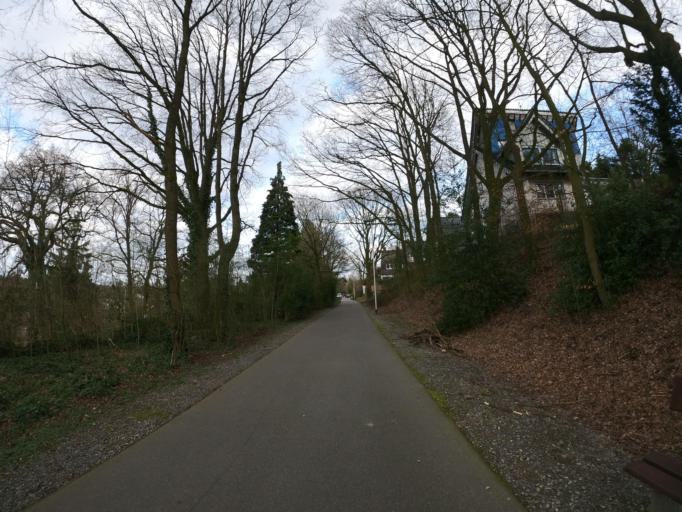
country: DE
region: North Rhine-Westphalia
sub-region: Regierungsbezirk Dusseldorf
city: Solingen
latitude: 51.1962
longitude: 7.0701
